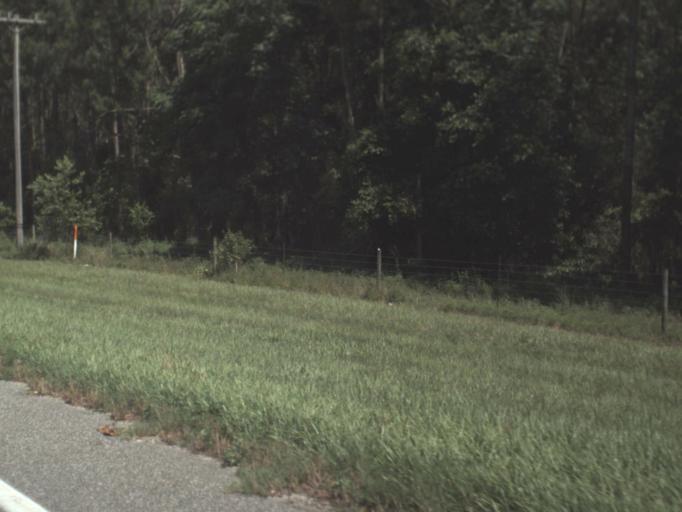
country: US
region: Florida
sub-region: Lafayette County
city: Mayo
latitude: 30.0532
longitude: -83.1229
